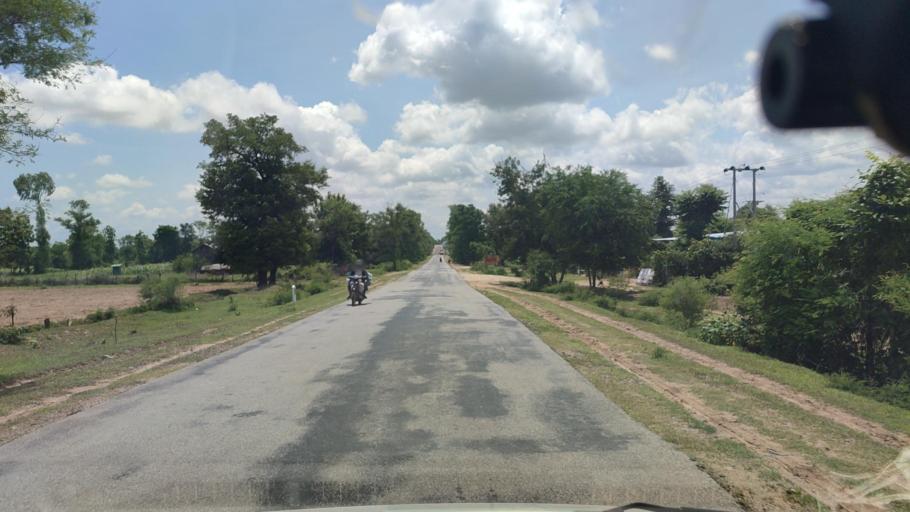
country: MM
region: Magway
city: Taungdwingyi
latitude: 20.2004
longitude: 95.3185
